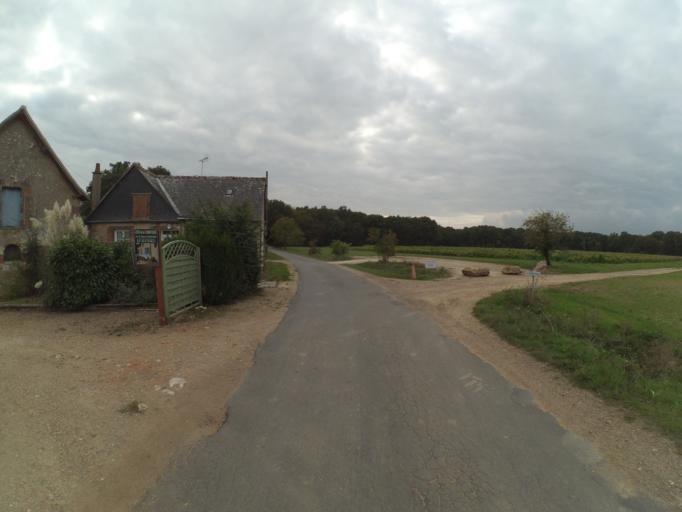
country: FR
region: Centre
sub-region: Departement d'Indre-et-Loire
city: Auzouer-en-Touraine
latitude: 47.5164
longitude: 0.9730
